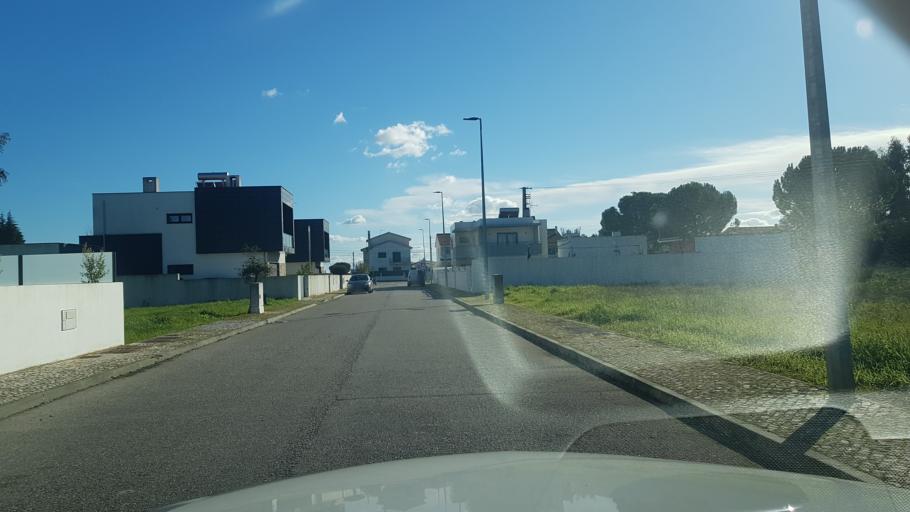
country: PT
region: Santarem
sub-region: Entroncamento
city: Entroncamento
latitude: 39.4787
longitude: -8.4781
